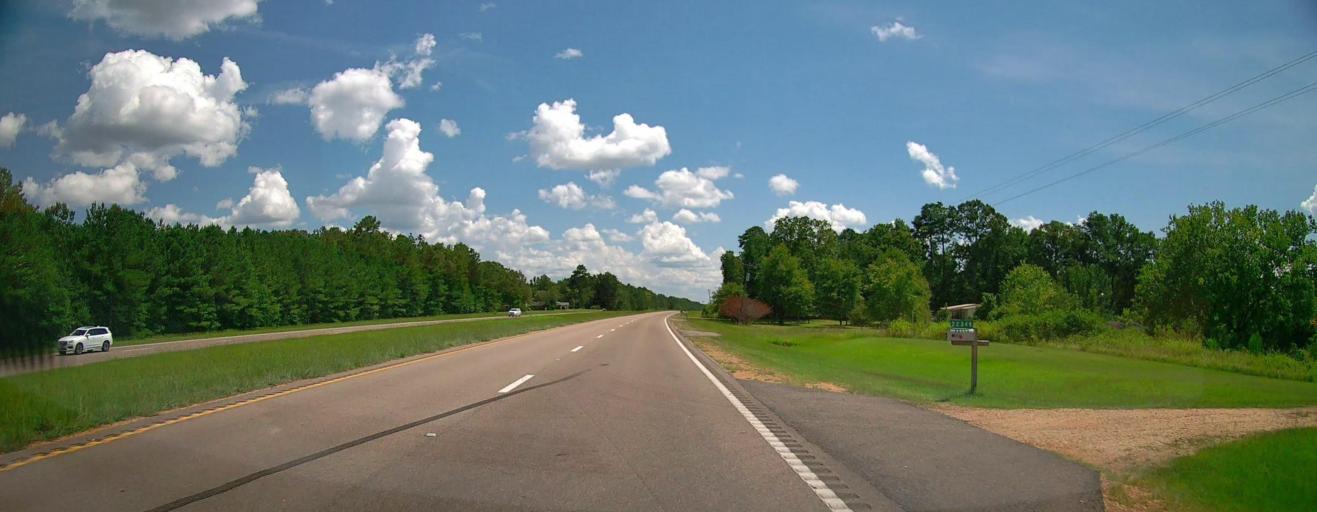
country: US
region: Mississippi
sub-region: Monroe County
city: Aberdeen
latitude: 33.9300
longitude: -88.5965
